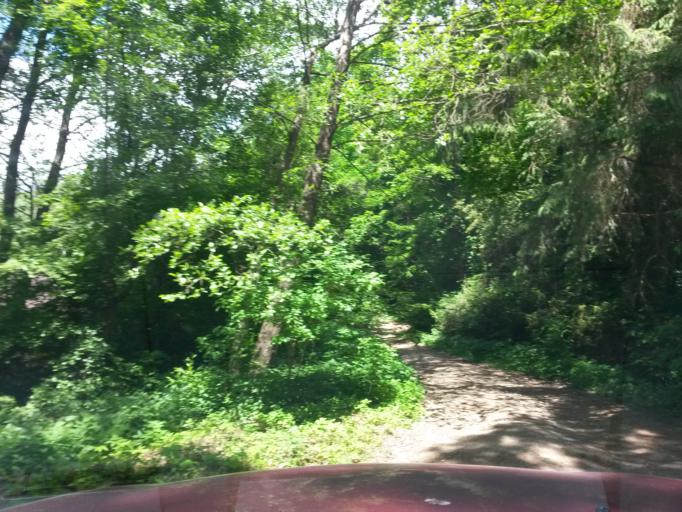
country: SK
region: Kosicky
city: Kosice
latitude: 48.7377
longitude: 21.1177
